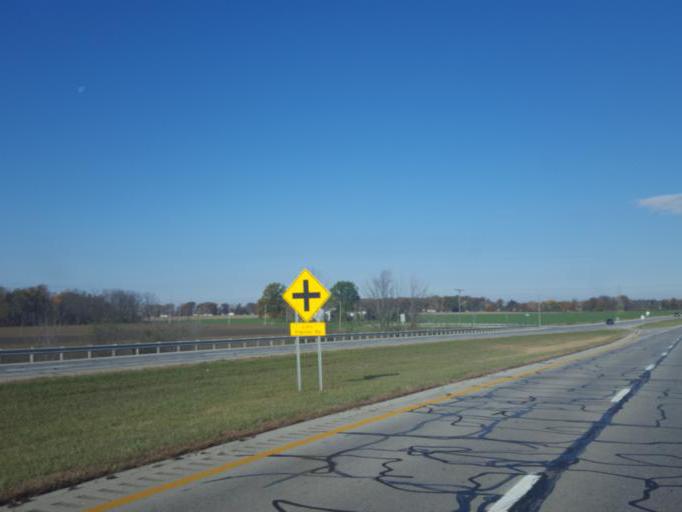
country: US
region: Ohio
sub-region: Marion County
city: Marion
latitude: 40.6501
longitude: -83.1036
